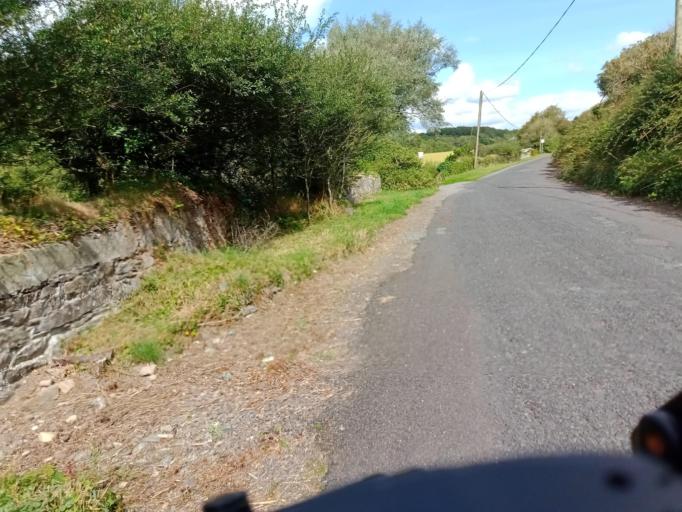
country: IE
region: Munster
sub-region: Waterford
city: Dungarvan
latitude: 52.1076
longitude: -7.5105
